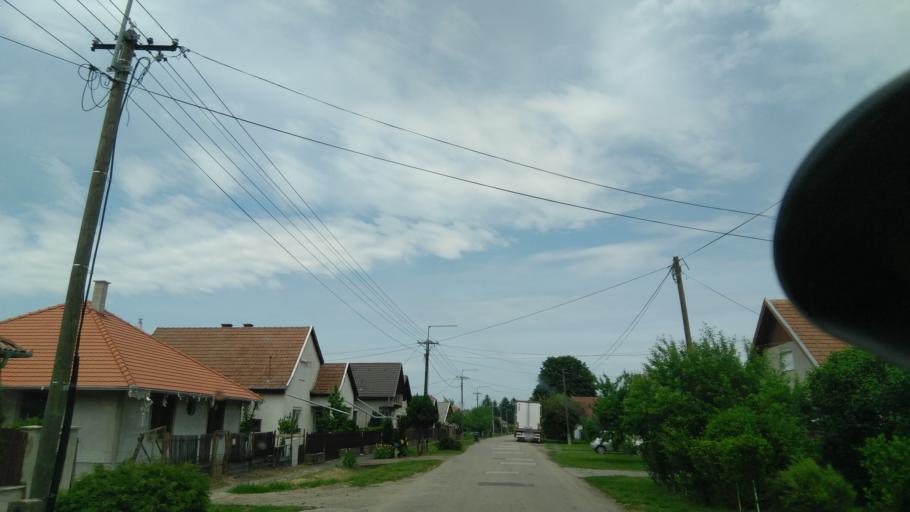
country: HU
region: Bekes
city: Fuzesgyarmat
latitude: 47.1025
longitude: 21.2055
